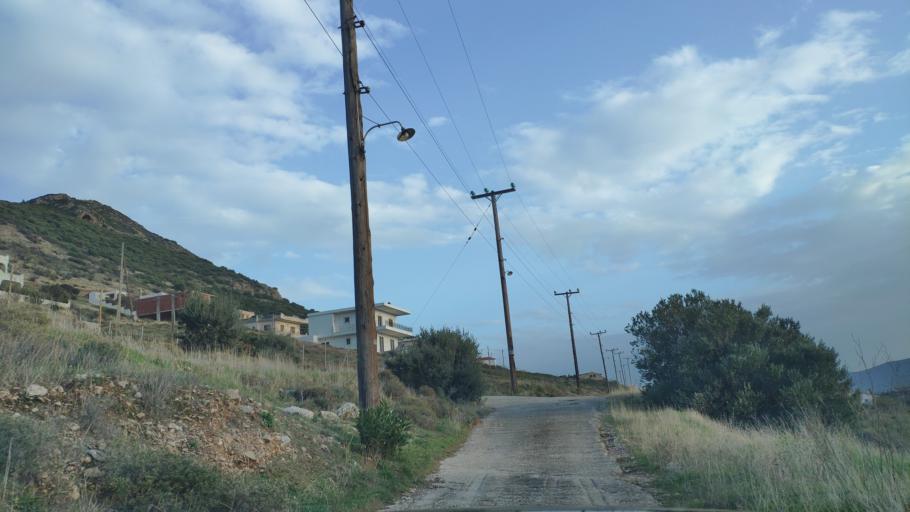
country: GR
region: Attica
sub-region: Nomarchia Anatolikis Attikis
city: Limin Mesoyaias
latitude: 37.9053
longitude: 24.0236
